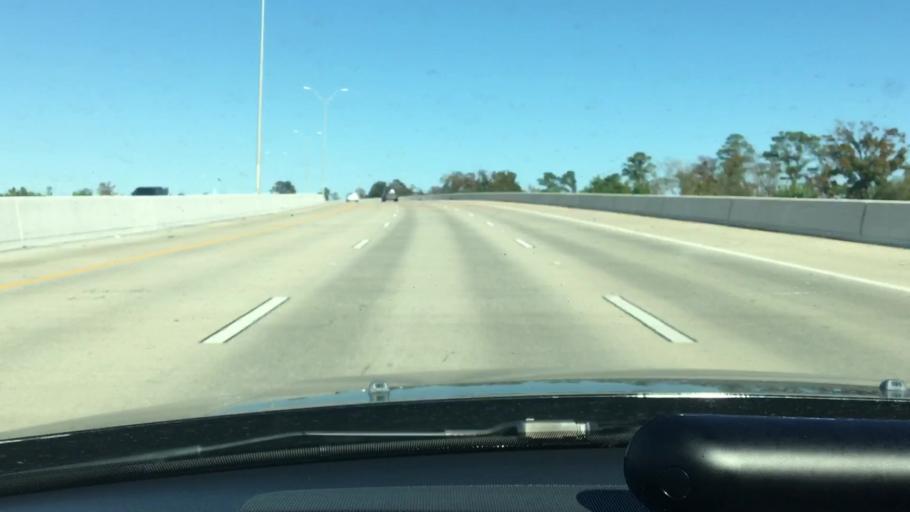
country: US
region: Texas
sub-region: Harris County
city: Atascocita
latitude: 29.9224
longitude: -95.1998
